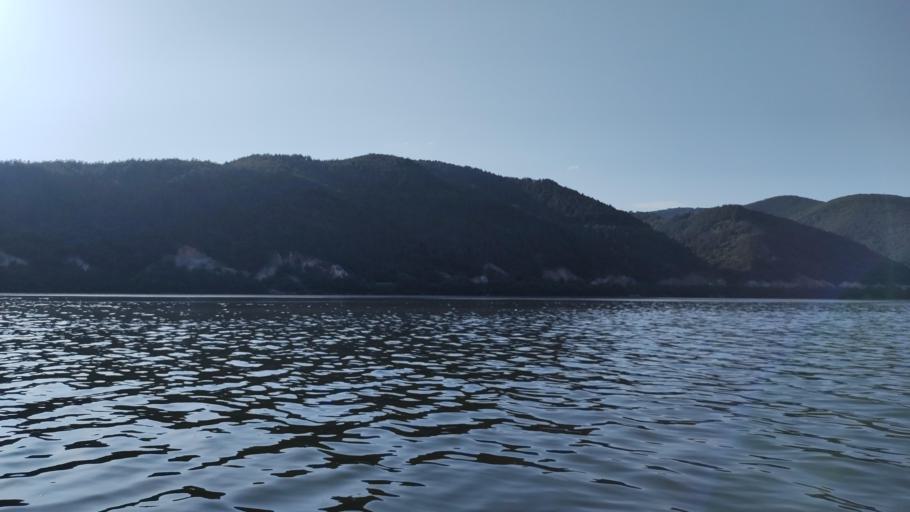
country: RO
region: Mehedinti
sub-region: Comuna Dubova
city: Dubova
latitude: 44.5292
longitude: 22.2114
